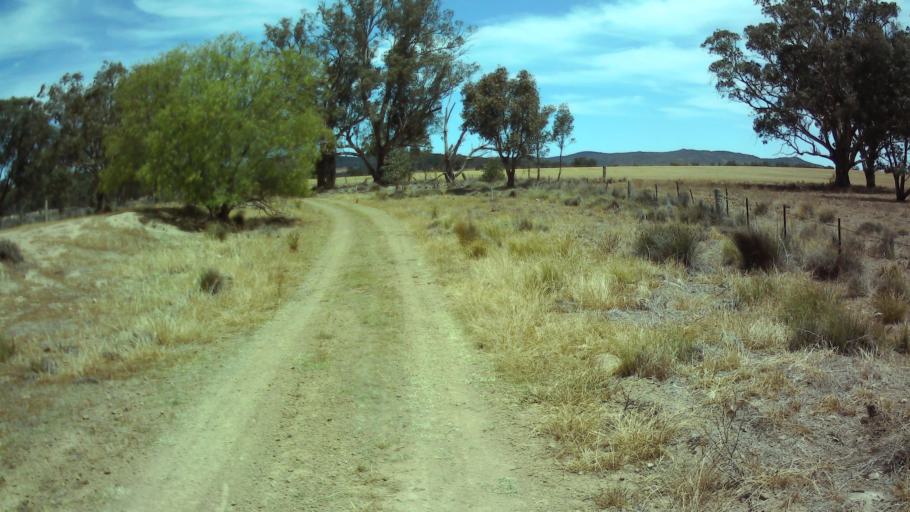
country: AU
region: New South Wales
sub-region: Weddin
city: Grenfell
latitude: -33.7607
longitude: 148.1452
